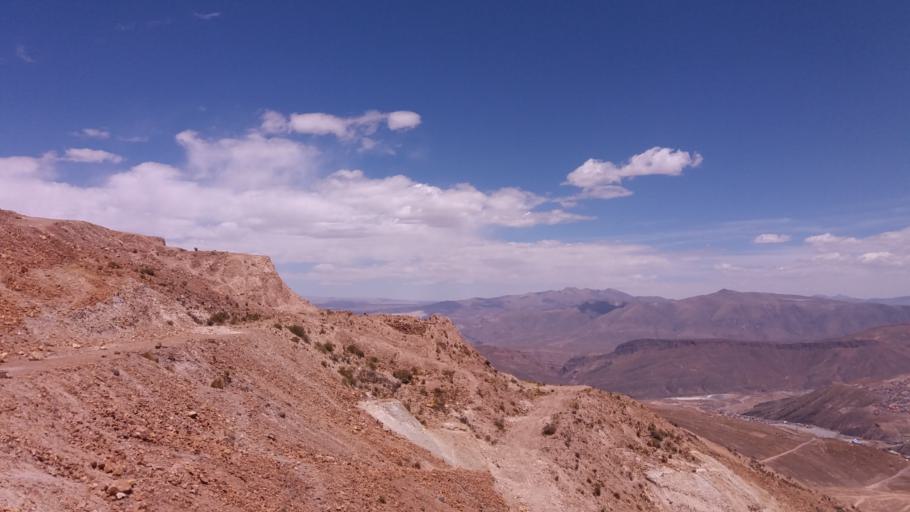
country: BO
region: Potosi
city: Potosi
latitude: -19.6127
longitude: -65.7479
